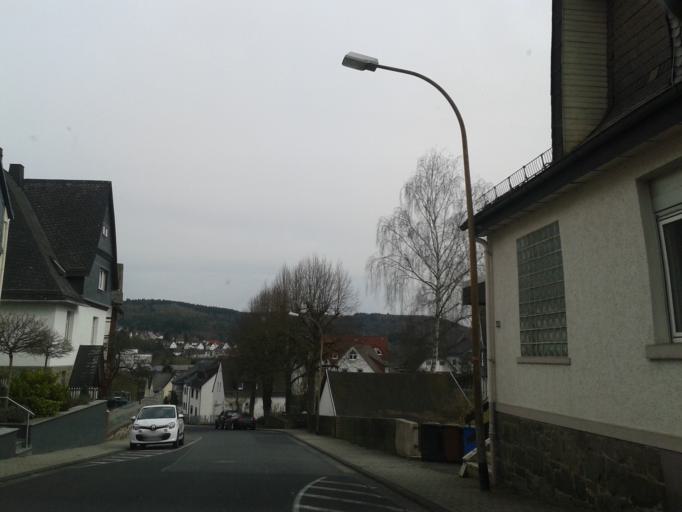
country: DE
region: Hesse
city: Herborn
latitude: 50.6803
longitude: 8.2990
